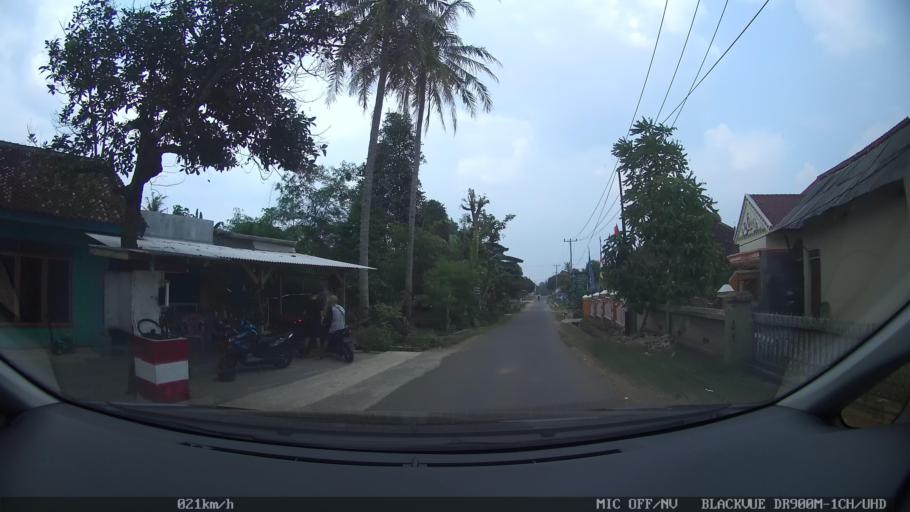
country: ID
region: Lampung
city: Gadingrejo
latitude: -5.3916
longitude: 105.0384
